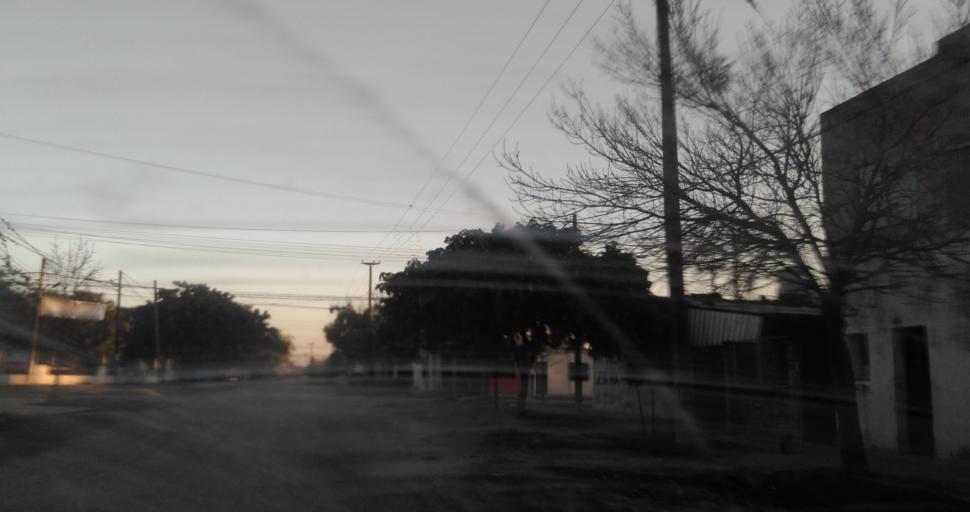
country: AR
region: Chaco
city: Resistencia
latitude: -27.4705
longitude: -58.9970
